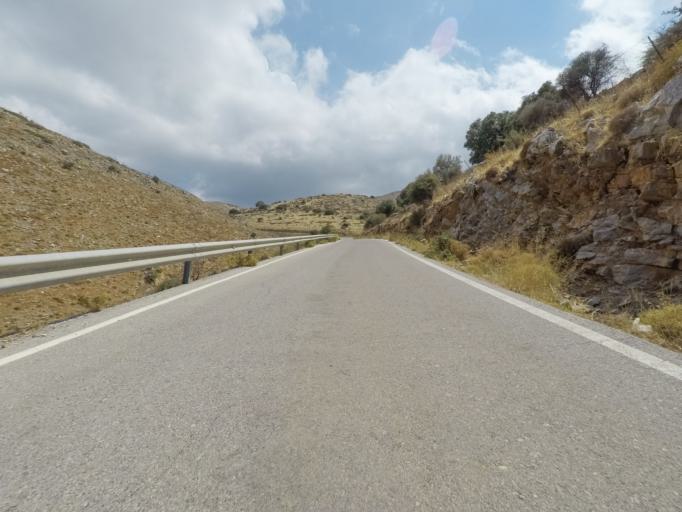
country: GR
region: Crete
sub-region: Nomos Lasithiou
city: Elounda
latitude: 35.3129
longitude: 25.6774
